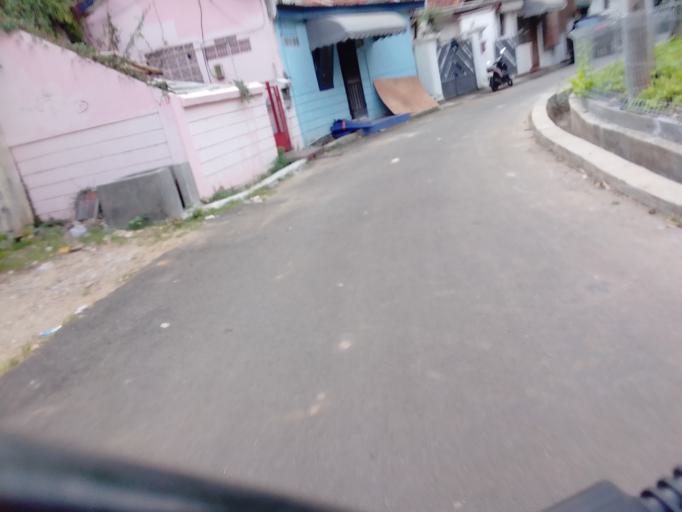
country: ID
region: Jakarta Raya
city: Jakarta
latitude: -6.2032
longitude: 106.8083
